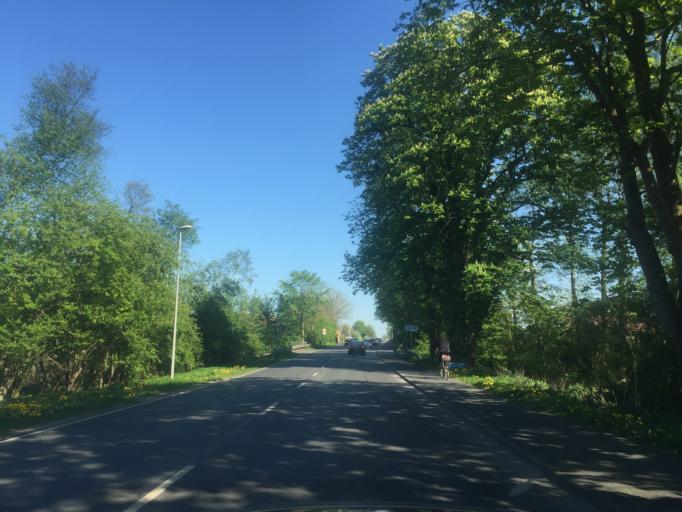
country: DK
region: South Denmark
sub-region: Odense Kommune
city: Hojby
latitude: 55.3423
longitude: 10.4262
